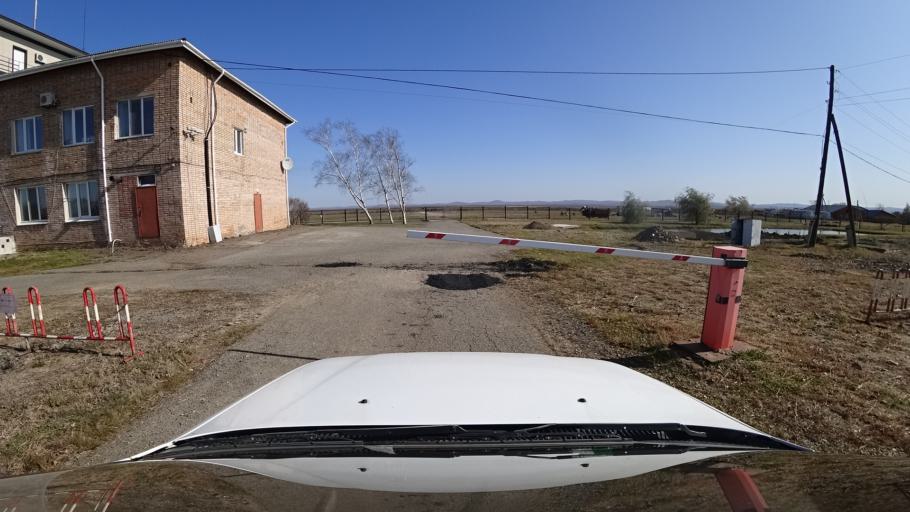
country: RU
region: Primorskiy
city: Dal'nerechensk
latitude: 45.8797
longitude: 133.7303
